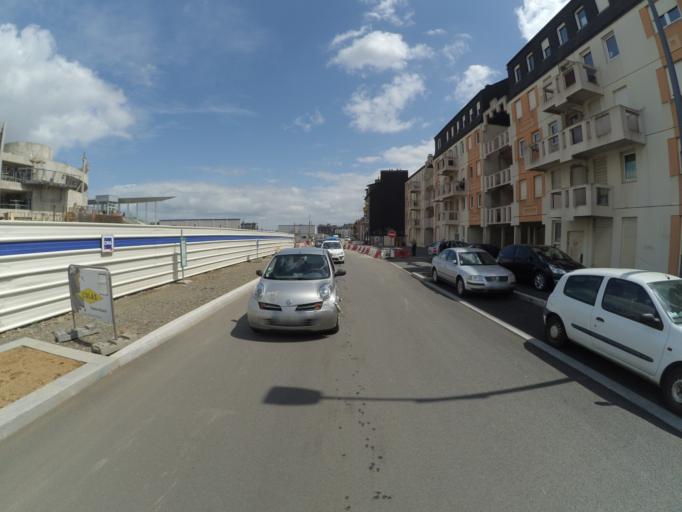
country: FR
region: Brittany
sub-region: Departement des Cotes-d'Armor
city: Saint-Brieuc
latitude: 48.5065
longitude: -2.7670
